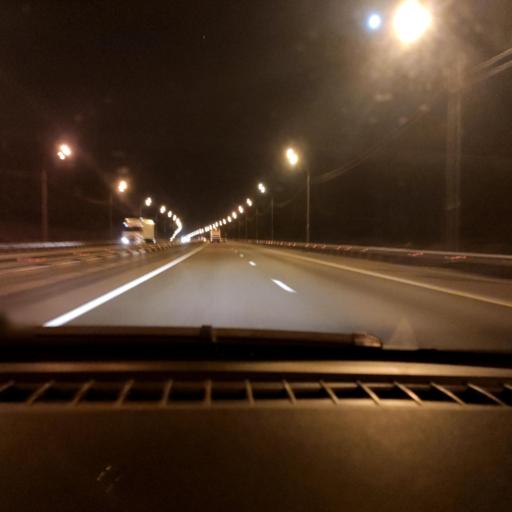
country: RU
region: Lipetsk
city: Khlevnoye
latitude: 52.2229
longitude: 39.1124
